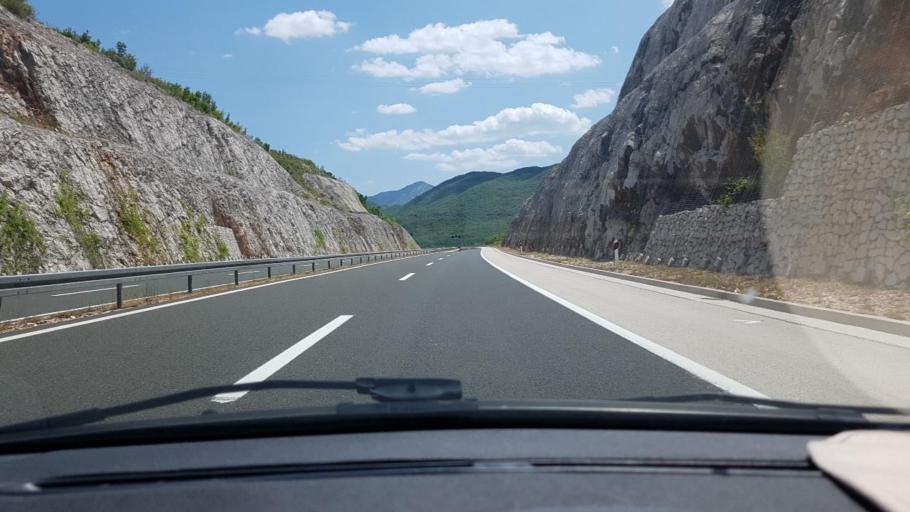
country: HR
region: Splitsko-Dalmatinska
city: Grubine
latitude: 43.3717
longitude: 17.0902
